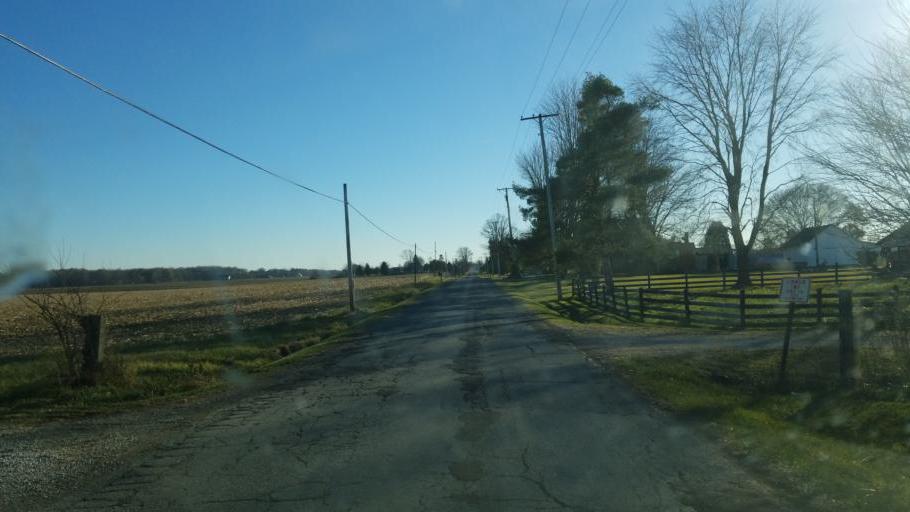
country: US
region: Ohio
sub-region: Morrow County
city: Cardington
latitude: 40.4814
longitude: -82.8951
